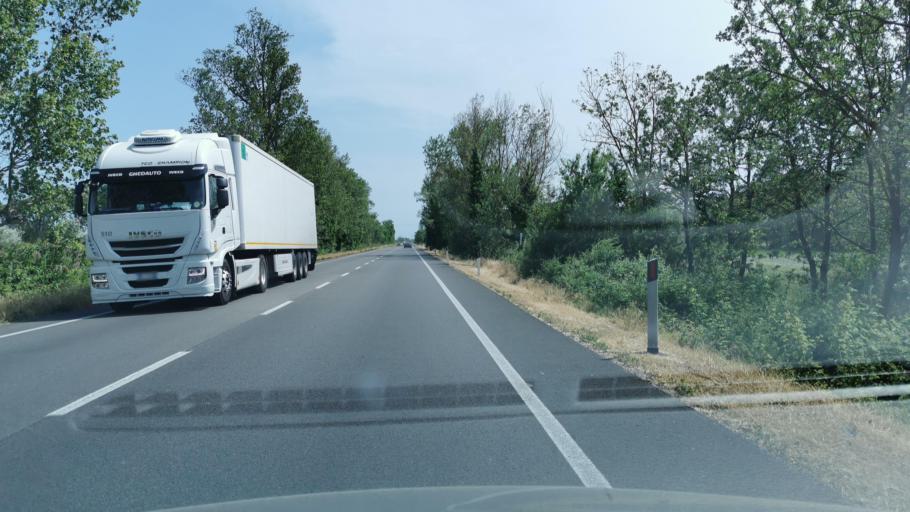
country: IT
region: Emilia-Romagna
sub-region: Provincia di Ferrara
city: Lido degli Estensi
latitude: 44.5927
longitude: 12.2500
